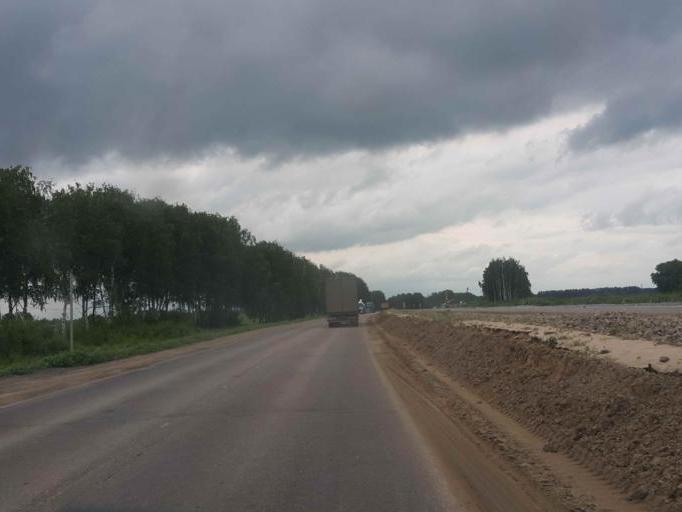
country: RU
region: Tambov
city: Selezni
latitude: 52.7874
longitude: 41.0226
